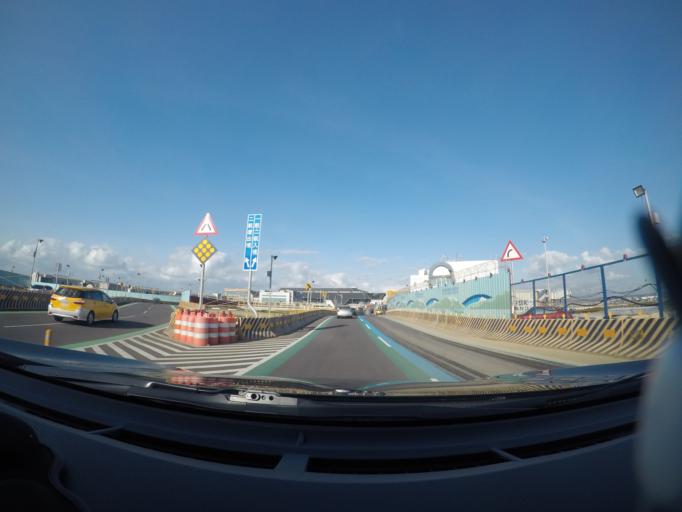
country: TW
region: Taiwan
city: Taoyuan City
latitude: 25.0732
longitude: 121.2298
